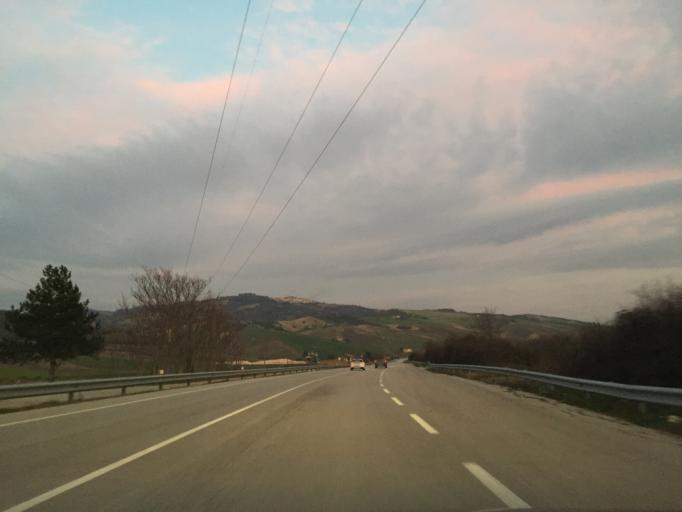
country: IT
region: Apulia
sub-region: Provincia di Foggia
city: Celenza Valfortore
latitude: 41.5266
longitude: 14.9590
